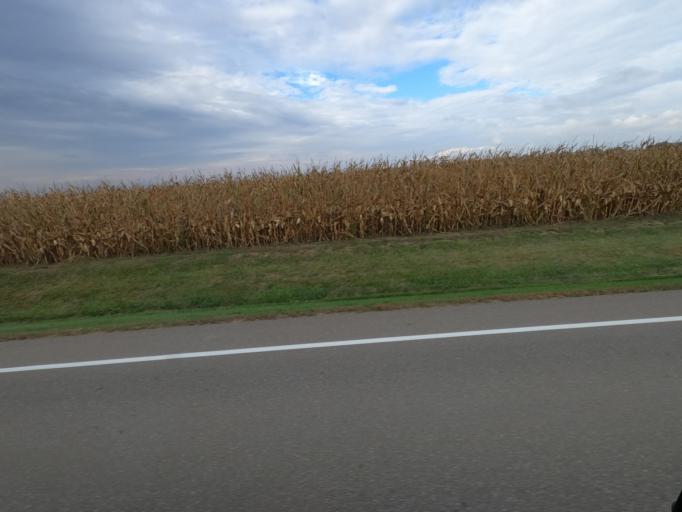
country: US
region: Iowa
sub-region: Henry County
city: Mount Pleasant
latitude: 40.7845
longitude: -91.5778
